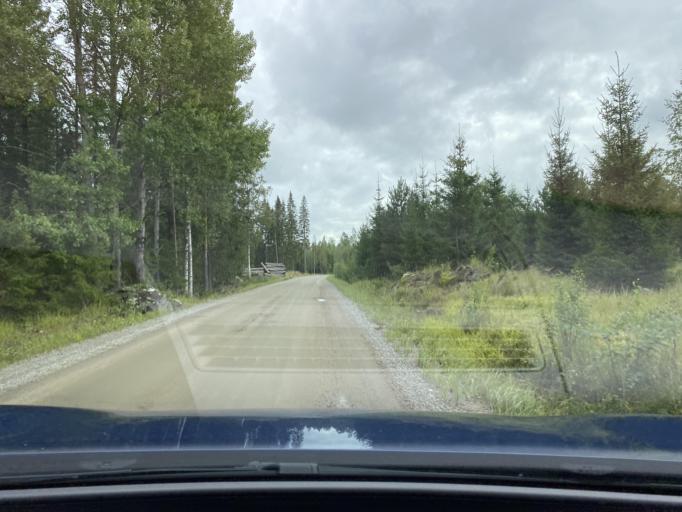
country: FI
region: Pirkanmaa
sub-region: Lounais-Pirkanmaa
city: Punkalaidun
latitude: 61.2100
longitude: 23.1742
